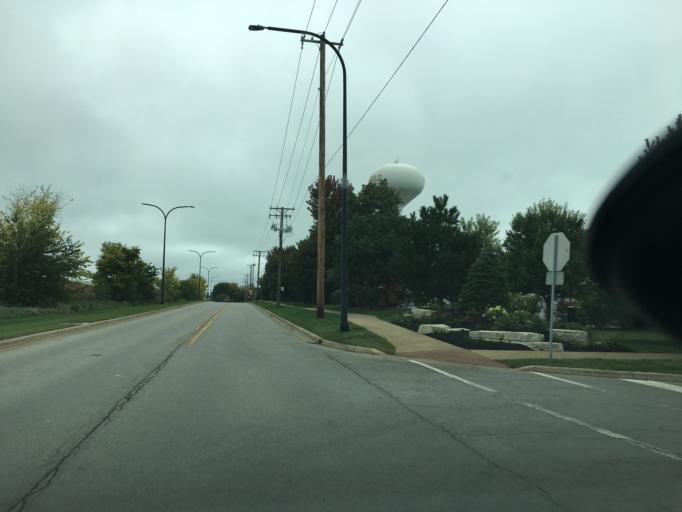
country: US
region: Illinois
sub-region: Will County
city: Plainfield
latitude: 41.6630
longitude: -88.2137
